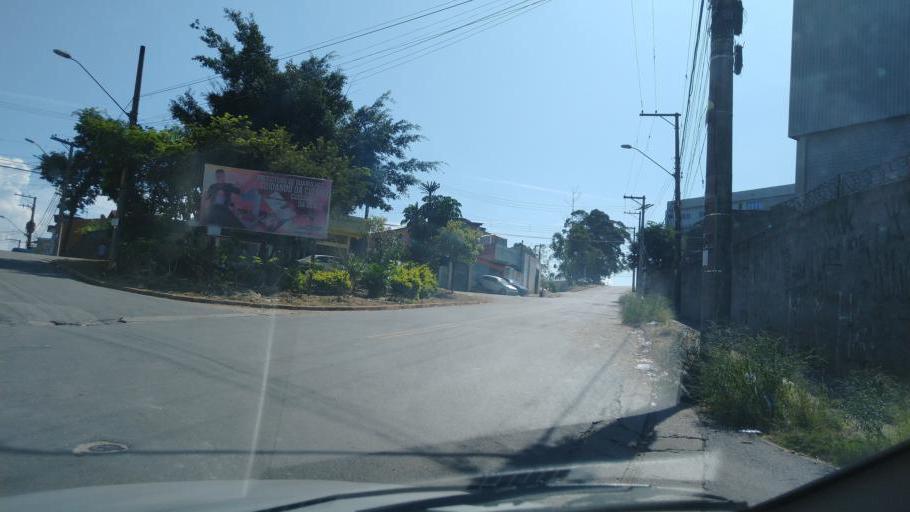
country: BR
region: Sao Paulo
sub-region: Aruja
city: Aruja
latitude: -23.4090
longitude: -46.3947
